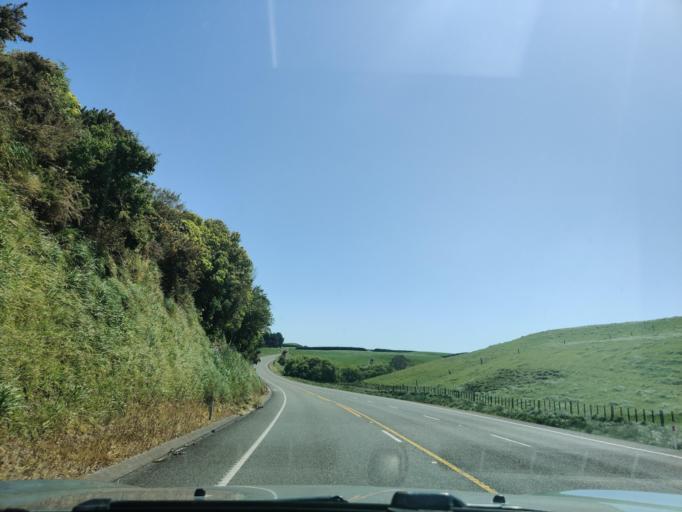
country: NZ
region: Taranaki
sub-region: South Taranaki District
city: Patea
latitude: -39.6874
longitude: 174.4204
